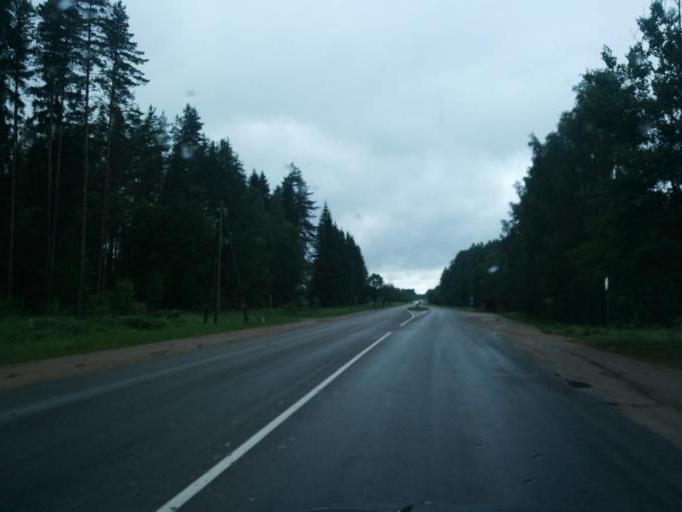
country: LV
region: Smiltene
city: Smiltene
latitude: 57.3899
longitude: 25.9735
